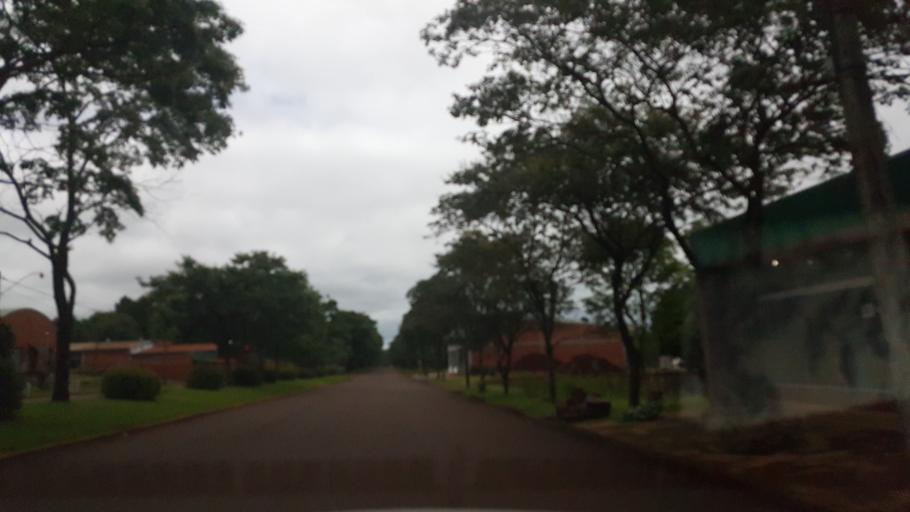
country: AR
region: Misiones
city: Ruiz de Montoya
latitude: -26.9720
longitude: -55.0517
